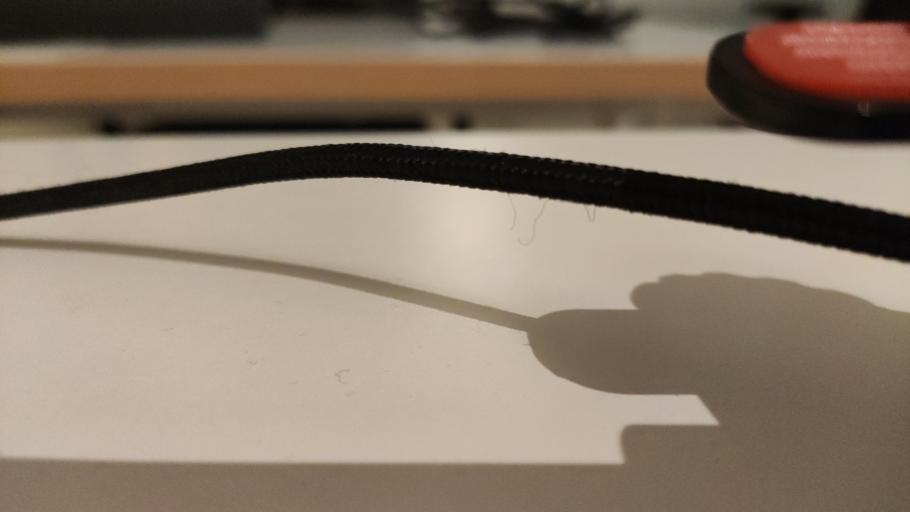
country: RU
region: Moskovskaya
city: Novoye
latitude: 55.6335
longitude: 38.9330
